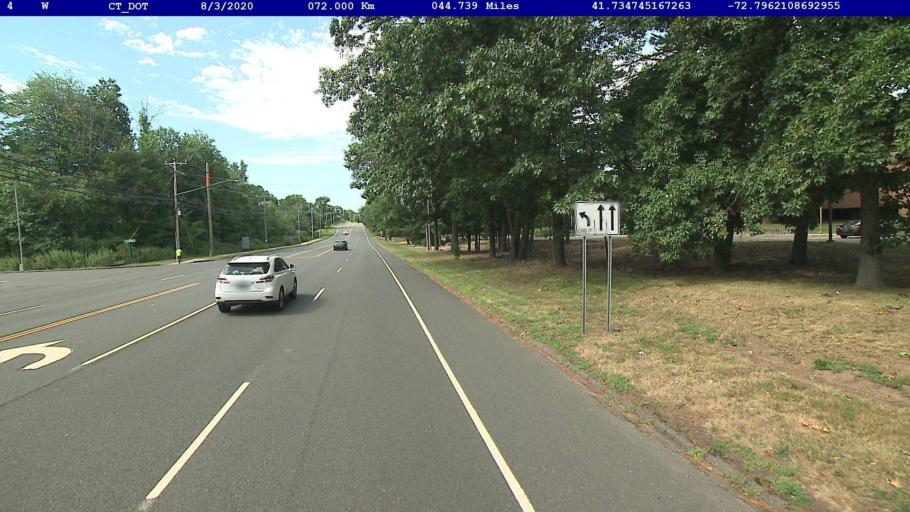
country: US
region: Connecticut
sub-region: Hartford County
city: Farmington
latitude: 41.7347
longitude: -72.7962
